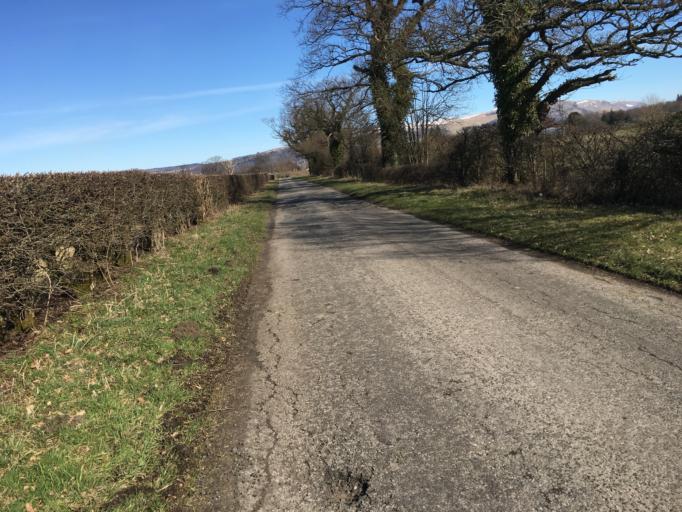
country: GB
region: Scotland
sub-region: Stirling
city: Bridge of Allan
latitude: 56.1331
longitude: -3.9845
